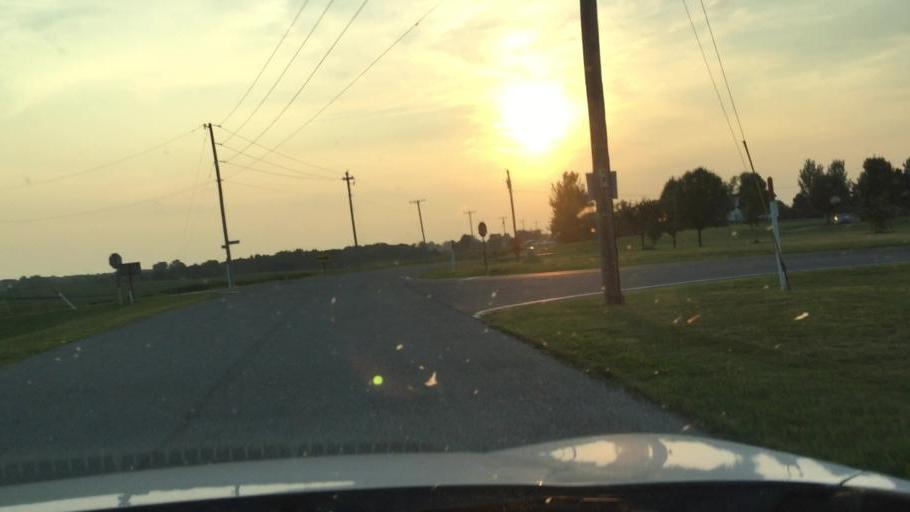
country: US
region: Ohio
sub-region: Madison County
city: Choctaw Lake
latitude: 39.9474
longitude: -83.5596
